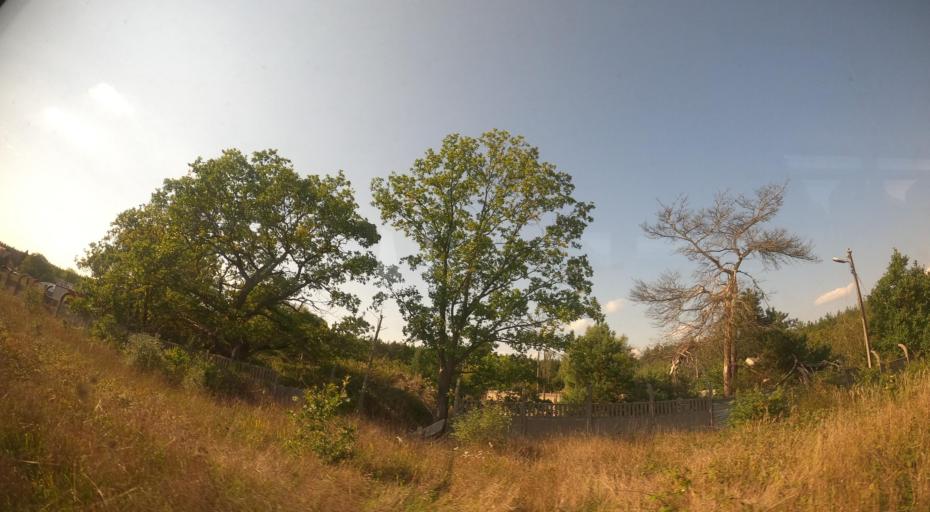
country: PL
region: Lubusz
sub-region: Powiat zielonogorski
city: Nowogrod Bobrzanski
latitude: 51.8146
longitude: 15.2466
